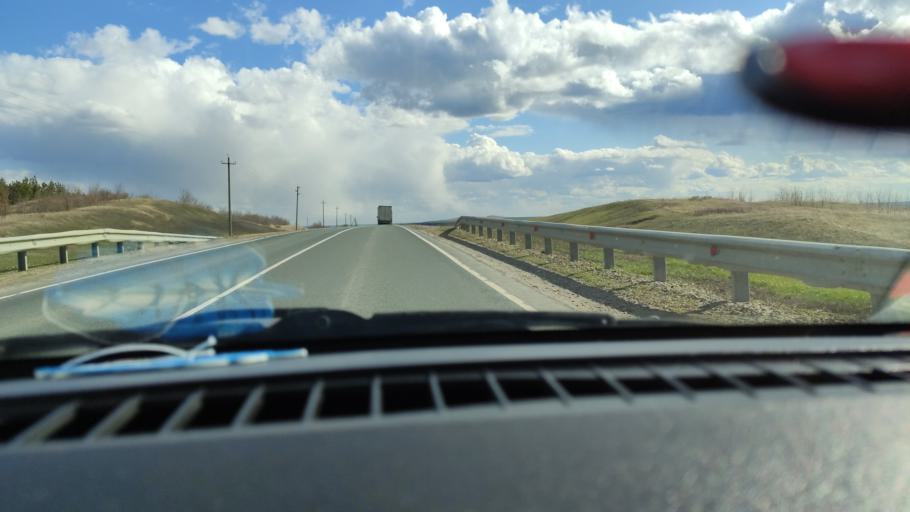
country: RU
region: Saratov
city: Alekseyevka
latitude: 52.2976
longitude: 47.9280
